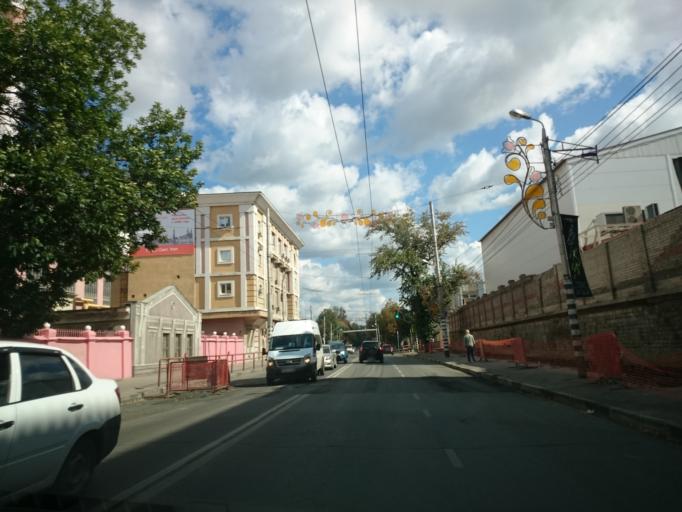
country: RU
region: Samara
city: Samara
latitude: 53.2019
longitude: 50.1020
